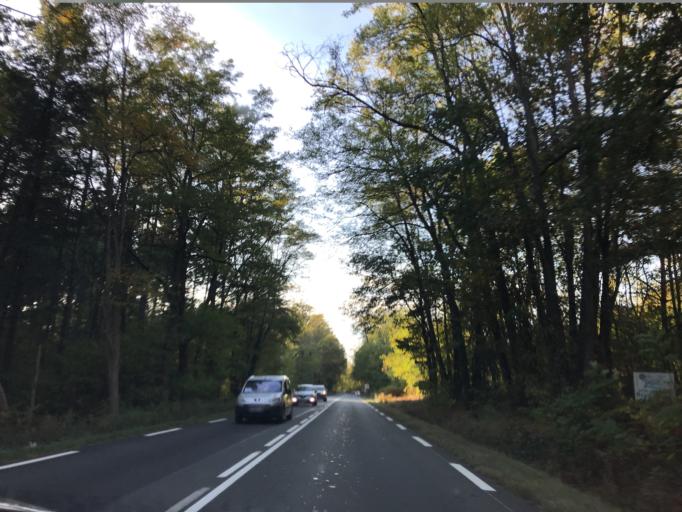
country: FR
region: Auvergne
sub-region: Departement du Puy-de-Dome
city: Paslieres
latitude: 45.9362
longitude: 3.4914
